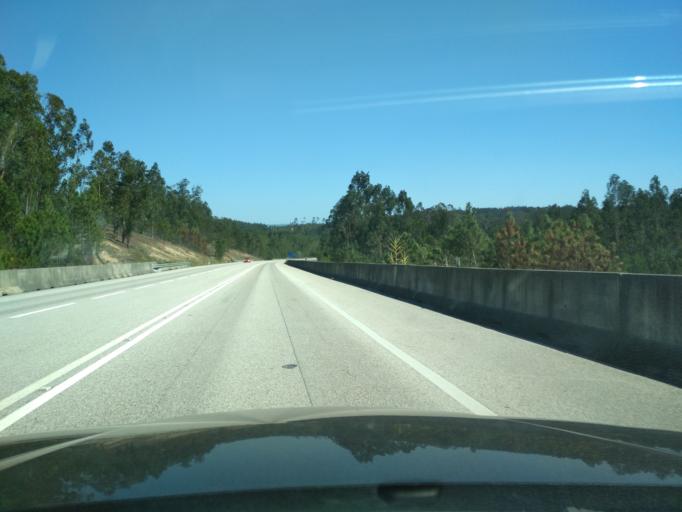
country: PT
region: Leiria
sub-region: Pombal
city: Lourical
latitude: 39.9881
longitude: -8.7734
